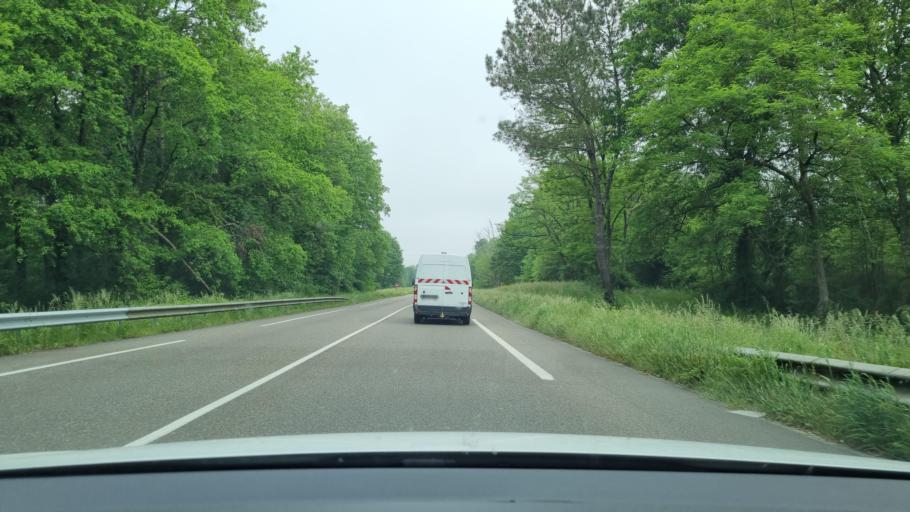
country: FR
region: Aquitaine
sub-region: Departement des Landes
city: Saint-Pierre-du-Mont
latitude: 43.8708
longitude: -0.5180
